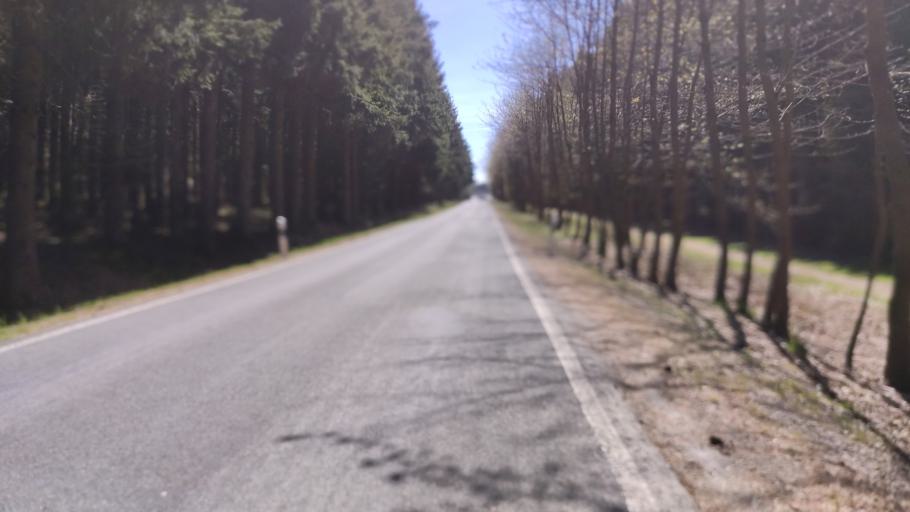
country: DE
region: Bavaria
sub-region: Upper Franconia
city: Tschirn
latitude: 50.4418
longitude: 11.4653
